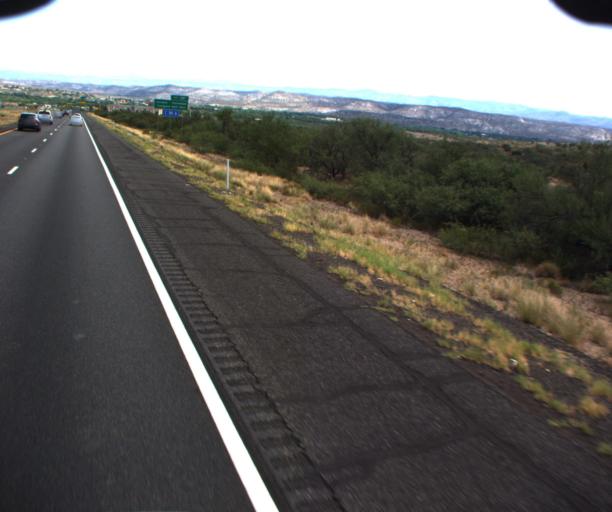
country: US
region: Arizona
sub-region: Yavapai County
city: Camp Verde
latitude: 34.5699
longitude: -111.8926
